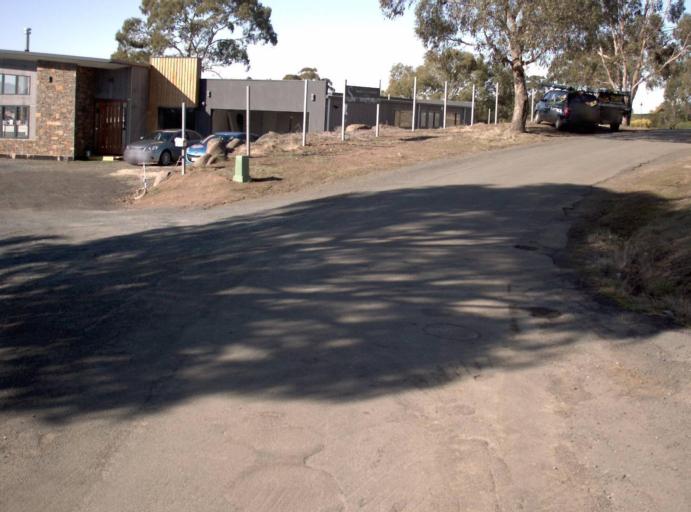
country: AU
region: Tasmania
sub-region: Launceston
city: Summerhill
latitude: -41.4747
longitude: 147.1553
